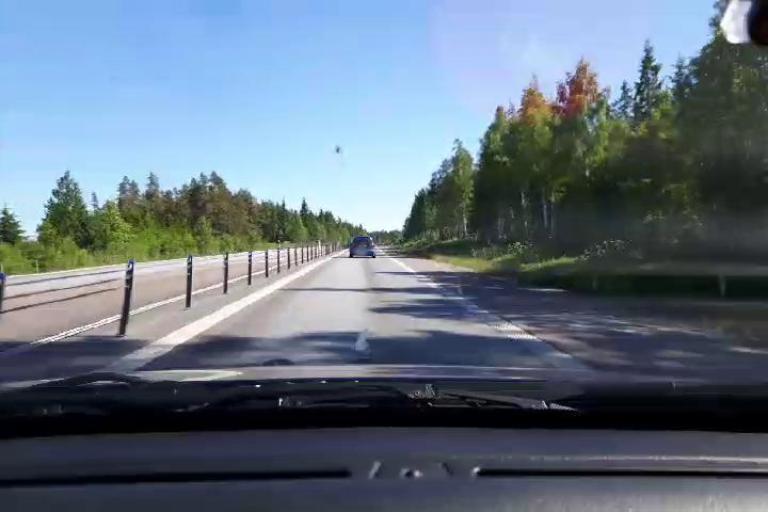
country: SE
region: Gaevleborg
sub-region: Gavle Kommun
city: Norrsundet
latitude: 60.8912
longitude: 17.0360
